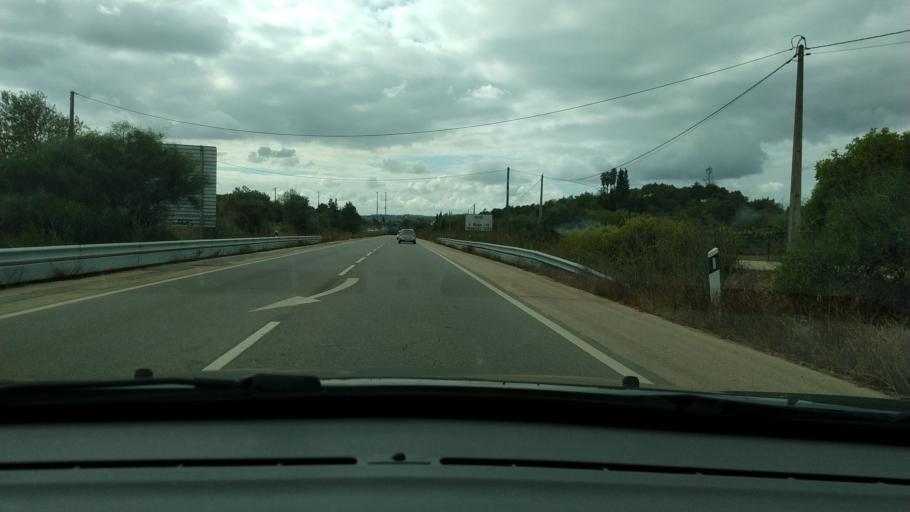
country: PT
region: Faro
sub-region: Lagos
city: Lagos
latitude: 37.0997
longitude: -8.7504
